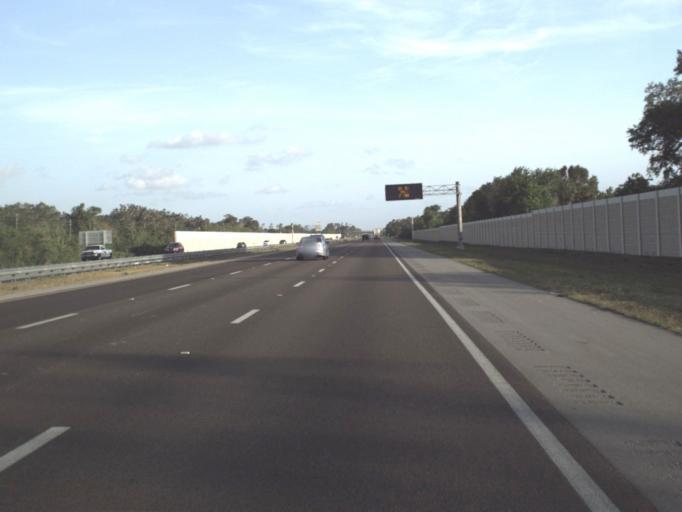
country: US
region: Florida
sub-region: Brevard County
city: Mims
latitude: 28.6504
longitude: -80.8634
